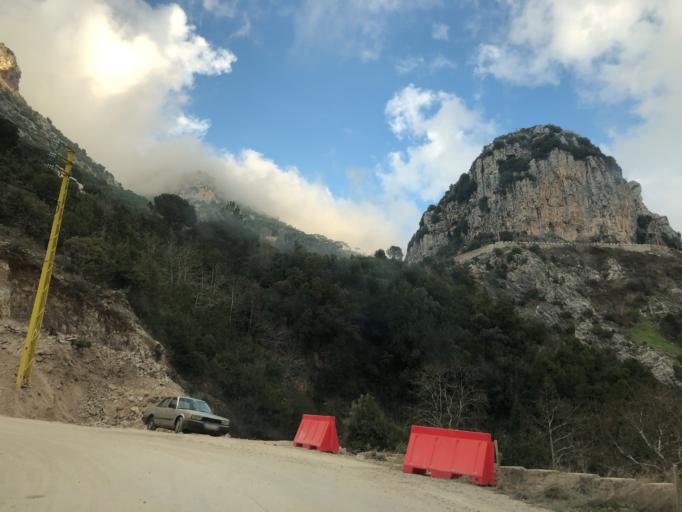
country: LB
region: Liban-Nord
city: Amioun
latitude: 34.1959
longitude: 35.8897
